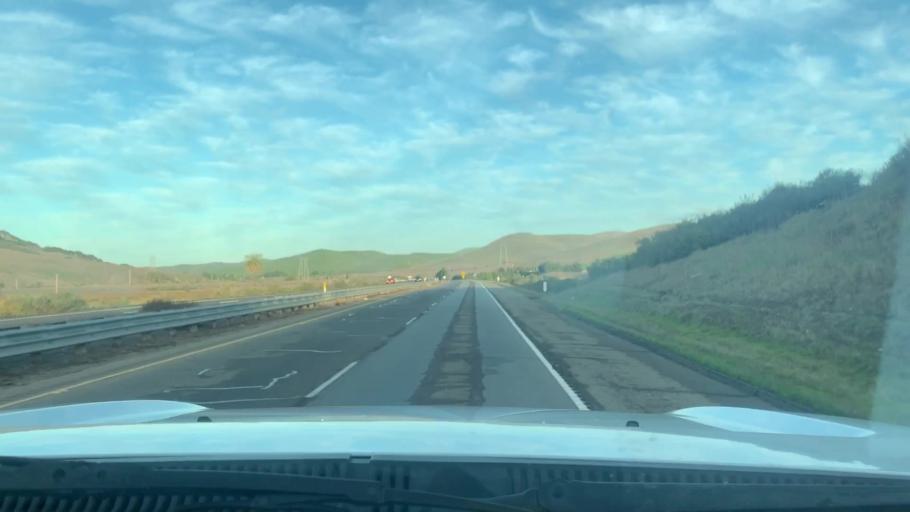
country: US
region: California
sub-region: San Luis Obispo County
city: Los Osos
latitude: 35.3412
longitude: -120.7627
